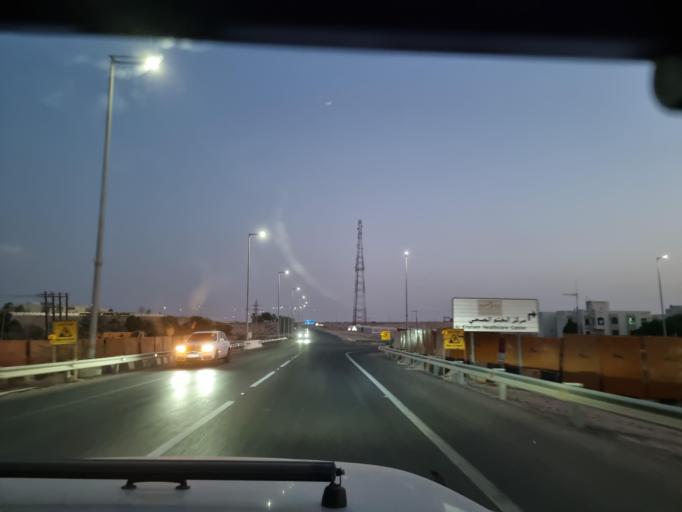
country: AE
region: Abu Dhabi
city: Abu Dhabi
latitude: 24.1865
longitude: 55.0031
